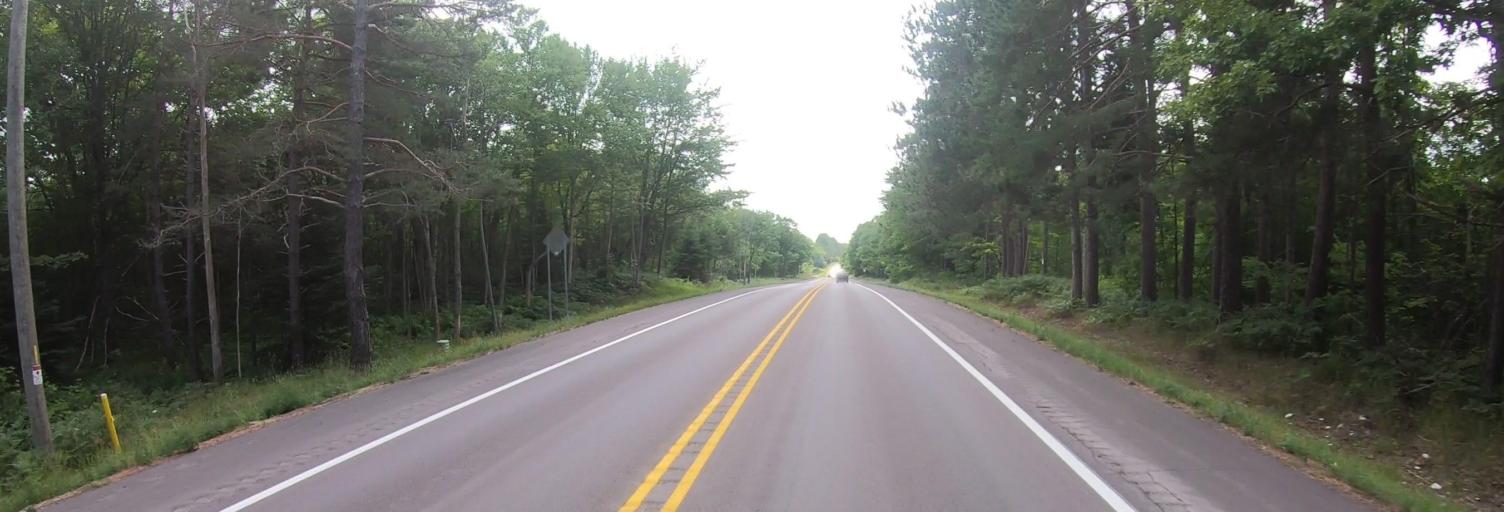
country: US
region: Michigan
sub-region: Houghton County
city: Hancock
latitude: 47.0541
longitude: -88.6648
